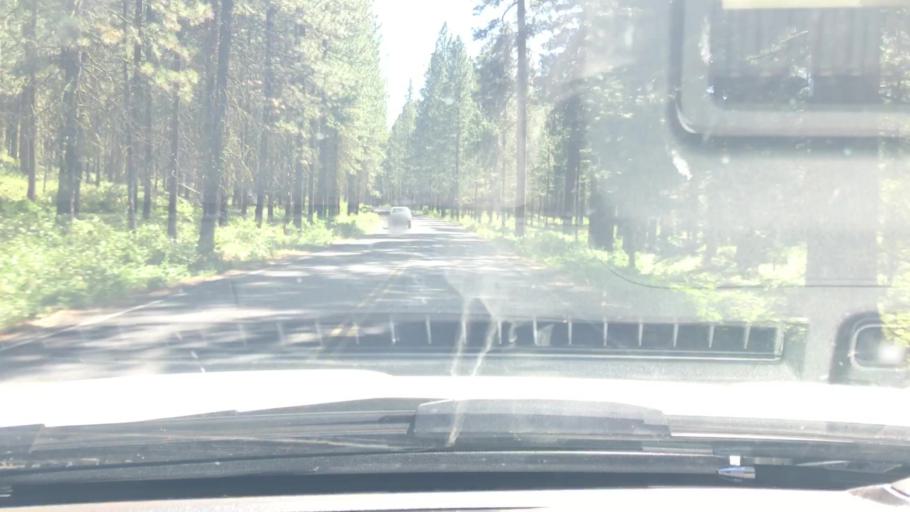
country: US
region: Oregon
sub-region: Deschutes County
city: Sisters
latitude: 44.4123
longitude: -121.6727
